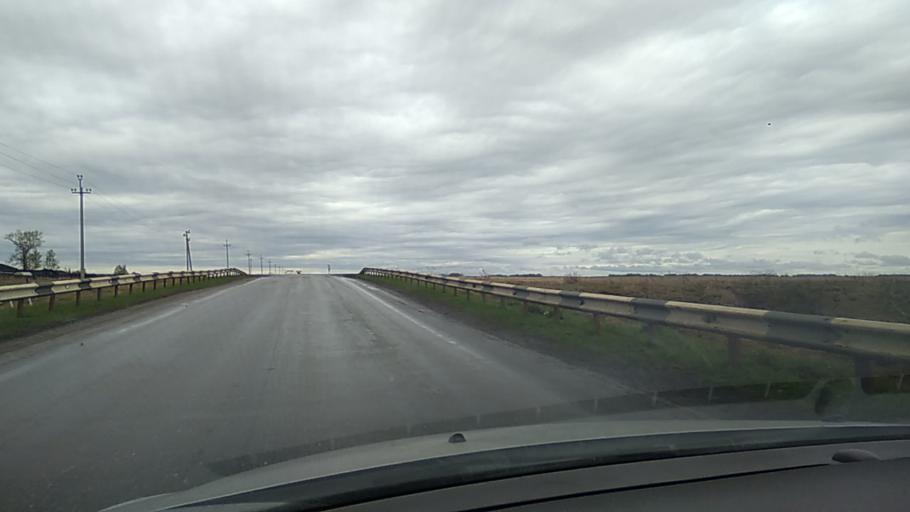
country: RU
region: Kurgan
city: Shatrovo
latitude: 56.3773
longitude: 64.8249
